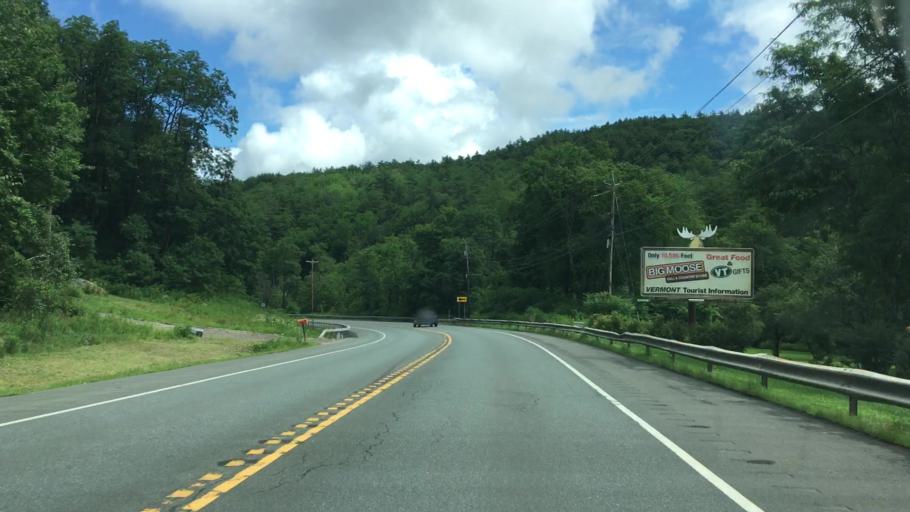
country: US
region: New York
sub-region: Rensselaer County
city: Hoosick Falls
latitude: 42.8416
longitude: -73.3709
